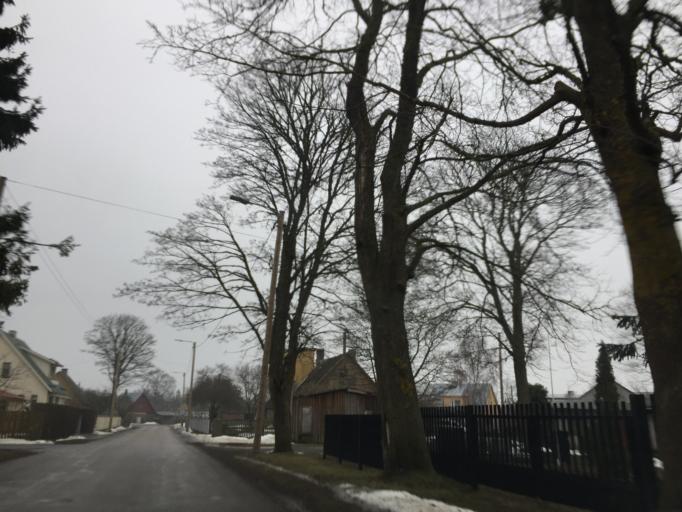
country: EE
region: Saare
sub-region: Kuressaare linn
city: Kuressaare
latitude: 58.2480
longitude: 22.4881
